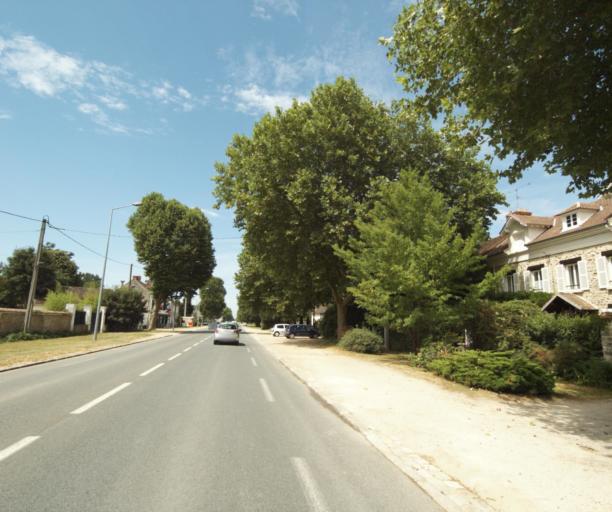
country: FR
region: Ile-de-France
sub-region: Departement de Seine-et-Marne
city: Chailly-en-Biere
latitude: 48.4693
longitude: 2.6046
